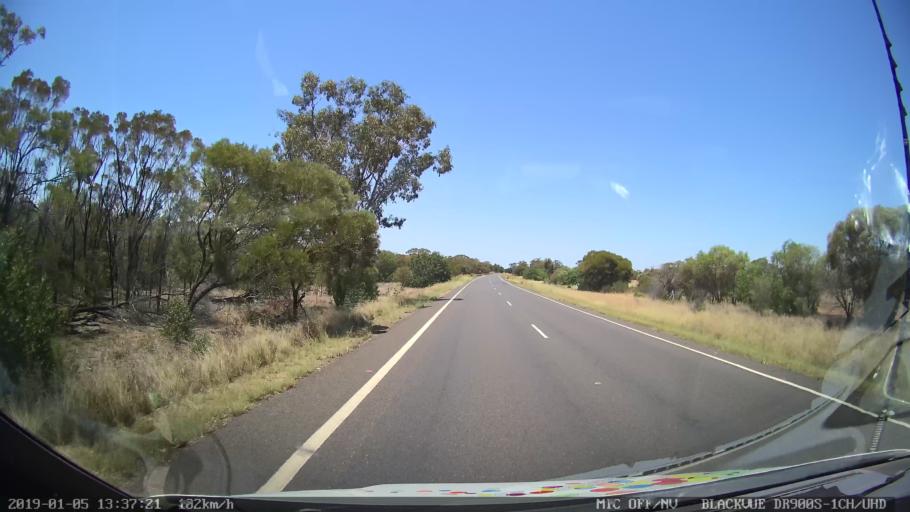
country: AU
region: New South Wales
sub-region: Gunnedah
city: Gunnedah
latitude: -30.9818
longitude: 150.1801
